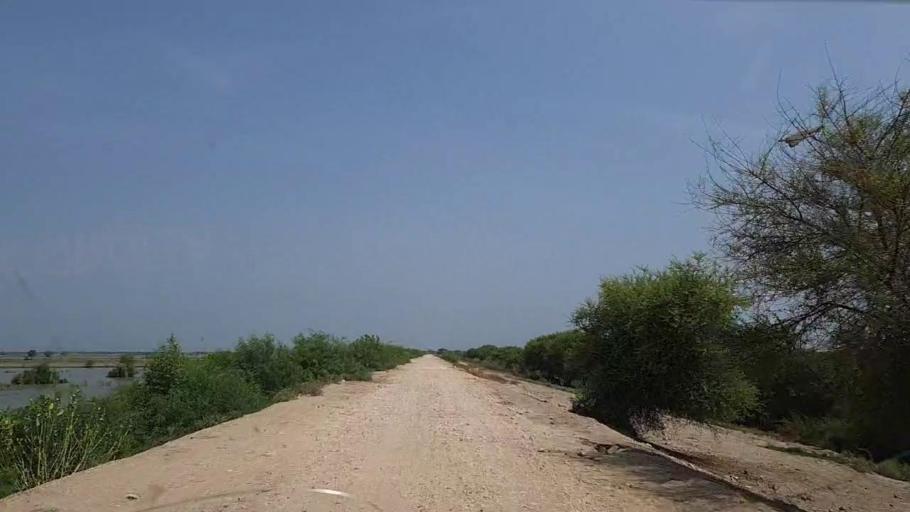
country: PK
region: Sindh
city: Ghotki
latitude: 28.1064
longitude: 69.3962
